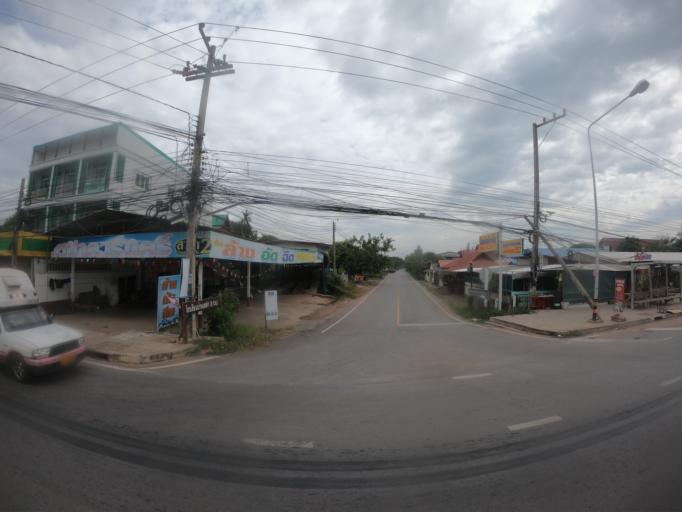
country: TH
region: Maha Sarakham
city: Kantharawichai
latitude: 16.3211
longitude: 103.2992
